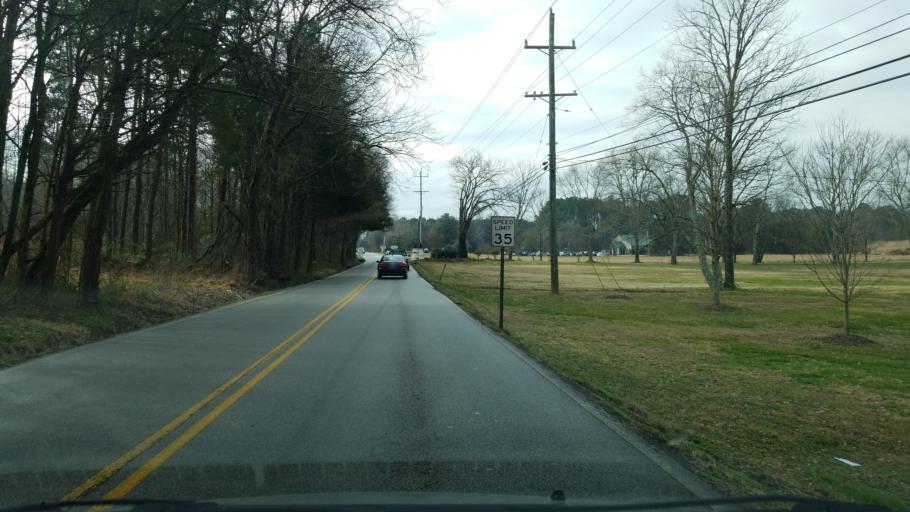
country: US
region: Tennessee
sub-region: Hamilton County
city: Collegedale
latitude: 35.0524
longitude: -85.0709
